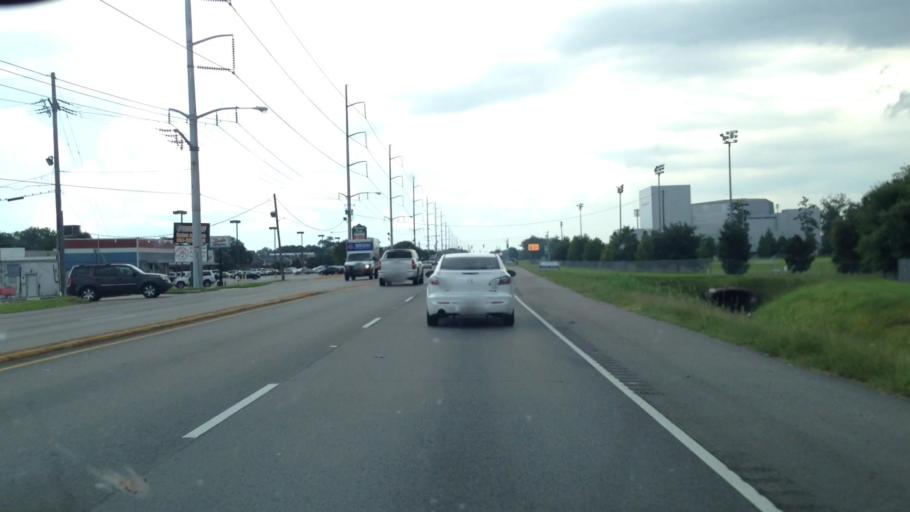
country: US
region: Louisiana
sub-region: Jefferson Parish
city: River Ridge
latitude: 29.9775
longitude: -90.2078
